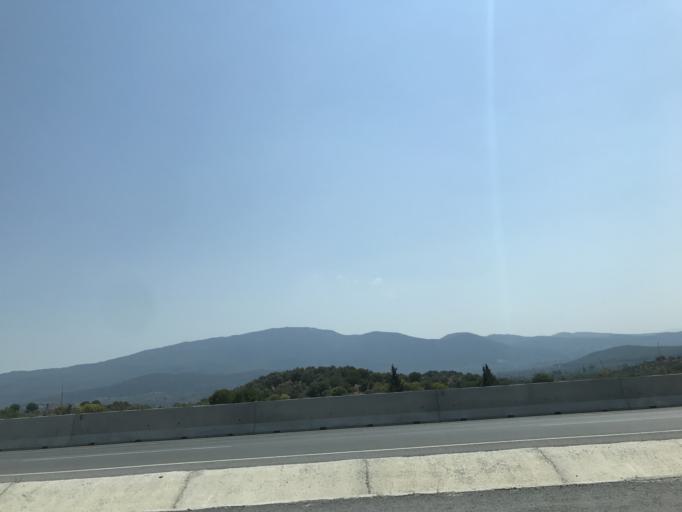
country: TR
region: Izmir
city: Selcuk
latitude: 37.8835
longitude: 27.4038
